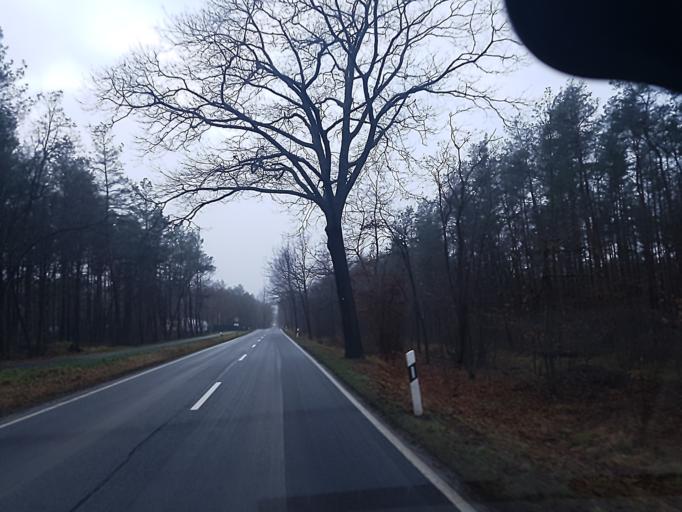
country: DE
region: Brandenburg
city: Finsterwalde
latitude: 51.5988
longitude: 13.7112
